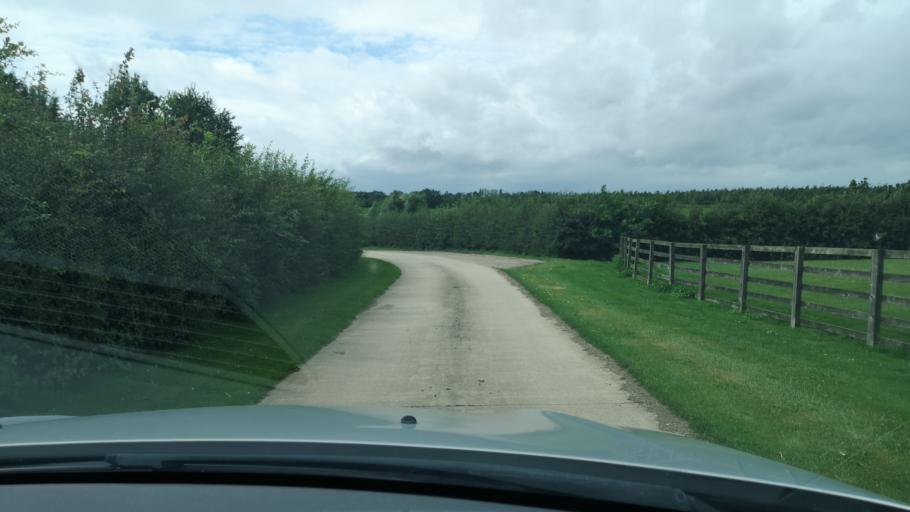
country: GB
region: England
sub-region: City and Borough of Wakefield
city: Darrington
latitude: 53.6848
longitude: -1.2576
